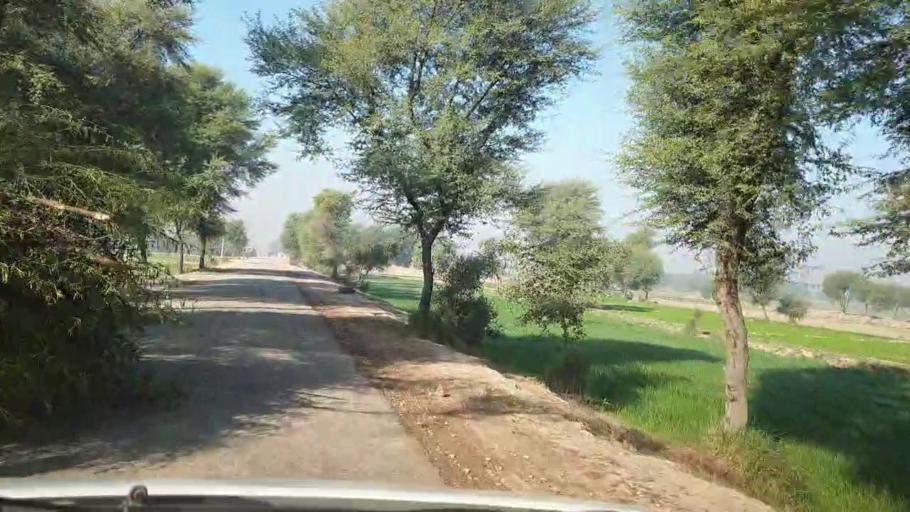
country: PK
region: Sindh
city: Dadu
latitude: 26.6766
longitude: 67.8235
